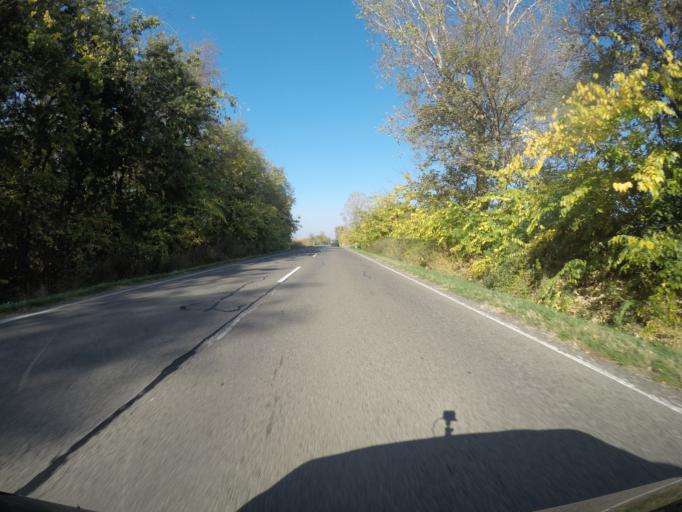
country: HU
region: Tolna
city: Tengelic
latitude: 46.5218
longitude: 18.6608
